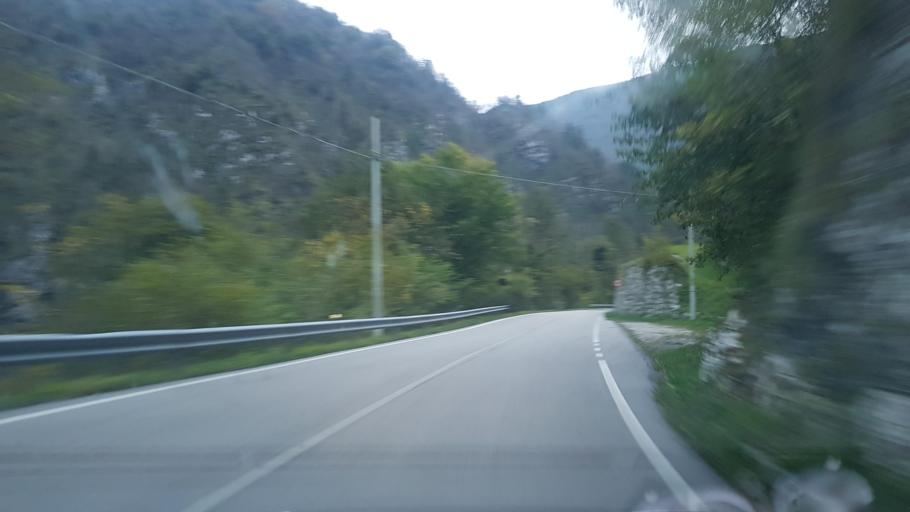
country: IT
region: Friuli Venezia Giulia
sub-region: Provincia di Pordenone
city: Anduins
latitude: 46.2685
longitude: 12.9554
